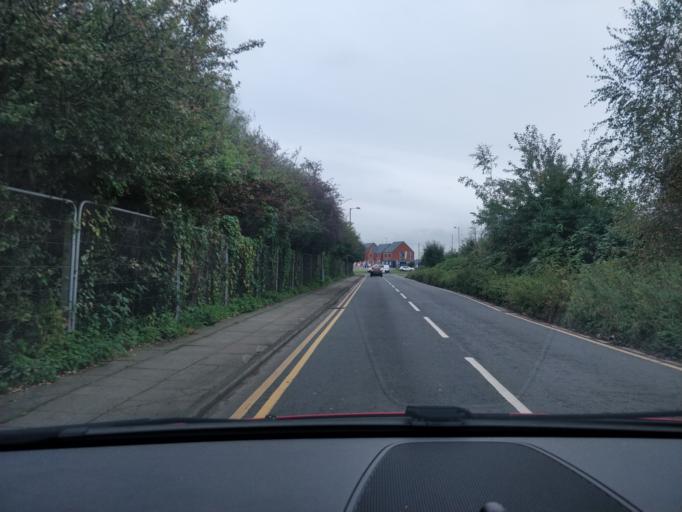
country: GB
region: England
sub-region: Sefton
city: Southport
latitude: 53.6323
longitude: -2.9853
